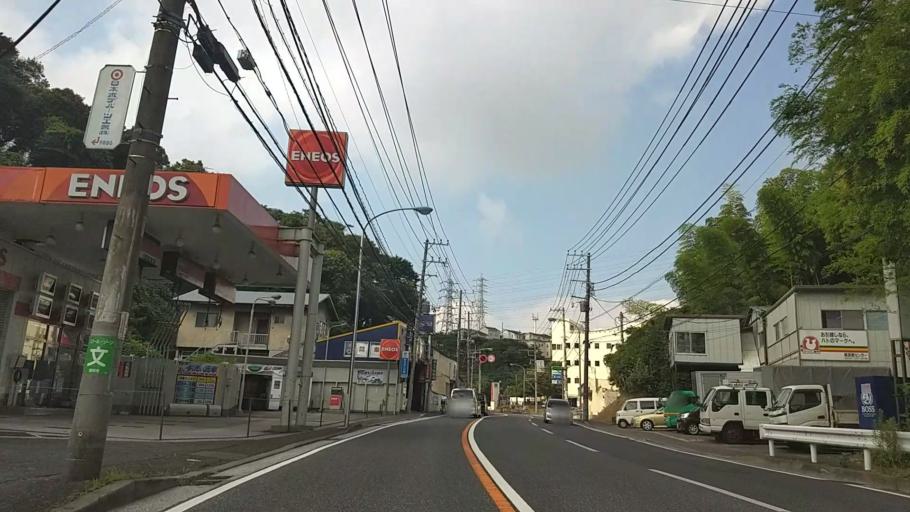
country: JP
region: Kanagawa
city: Yokohama
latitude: 35.4420
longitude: 139.5760
